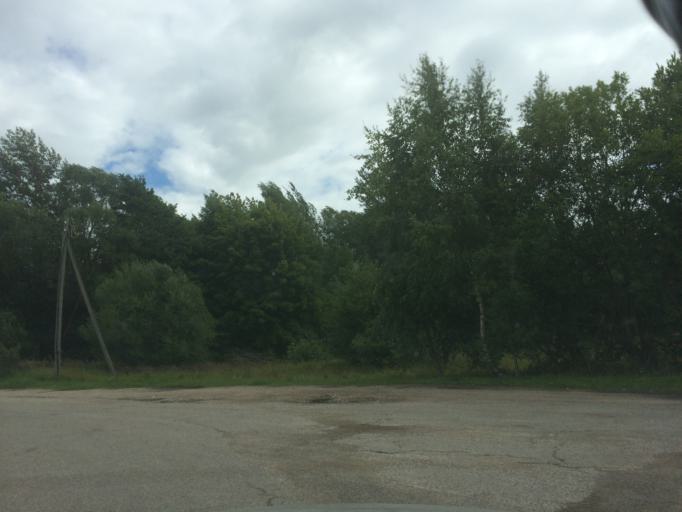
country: LV
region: Rezekne
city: Rezekne
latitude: 56.4885
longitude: 27.3135
